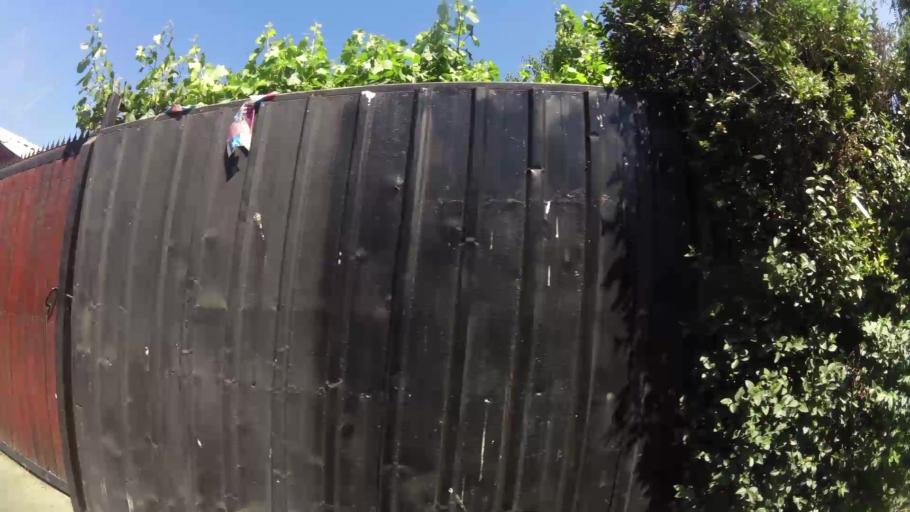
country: CL
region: Santiago Metropolitan
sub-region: Provincia de Maipo
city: San Bernardo
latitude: -33.6238
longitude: -70.6996
